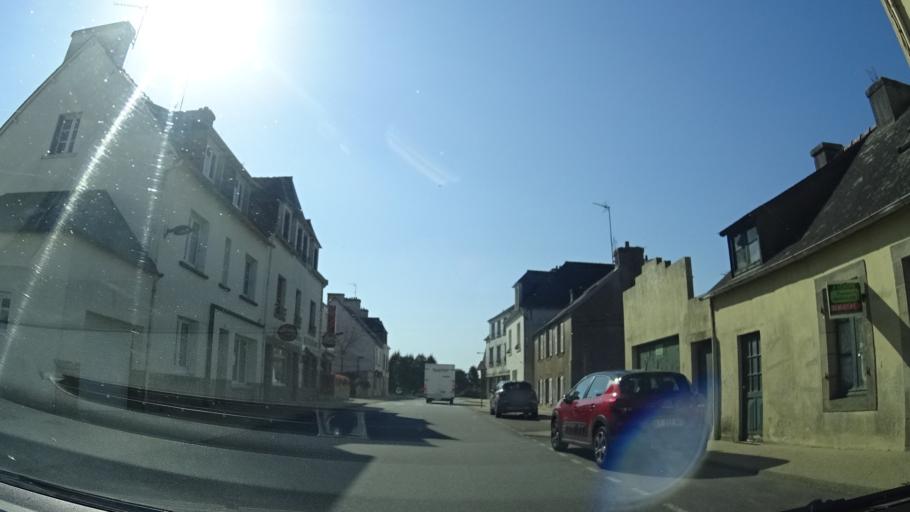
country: FR
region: Brittany
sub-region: Departement du Finistere
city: Cast
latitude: 48.1572
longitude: -4.1393
